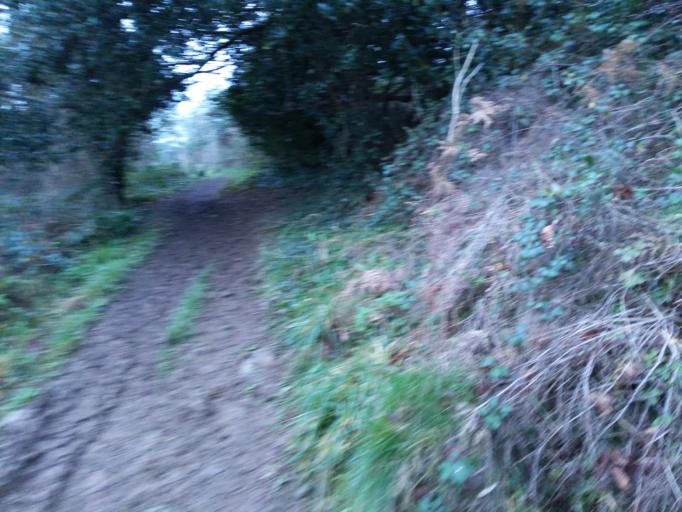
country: GB
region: England
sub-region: Cornwall
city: Fowey
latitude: 50.3365
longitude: -4.6181
